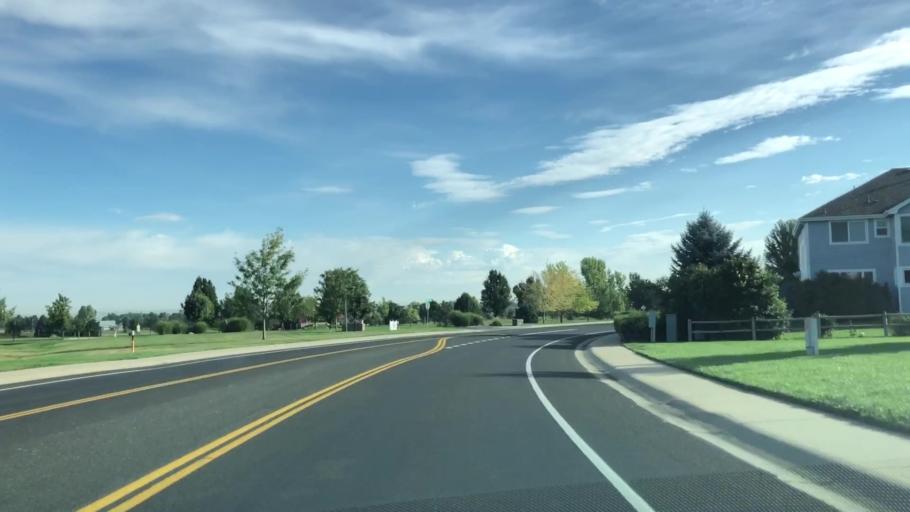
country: US
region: Colorado
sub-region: Weld County
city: Windsor
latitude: 40.4731
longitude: -104.9792
